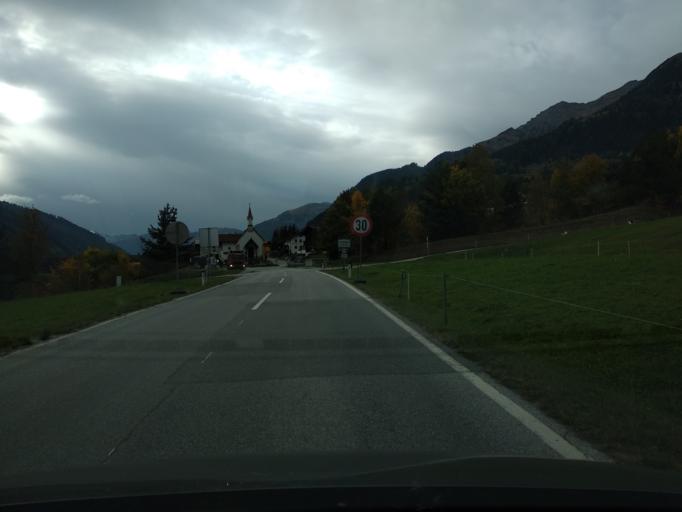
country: AT
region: Tyrol
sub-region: Politischer Bezirk Landeck
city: Flirsch
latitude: 47.1498
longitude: 10.3491
